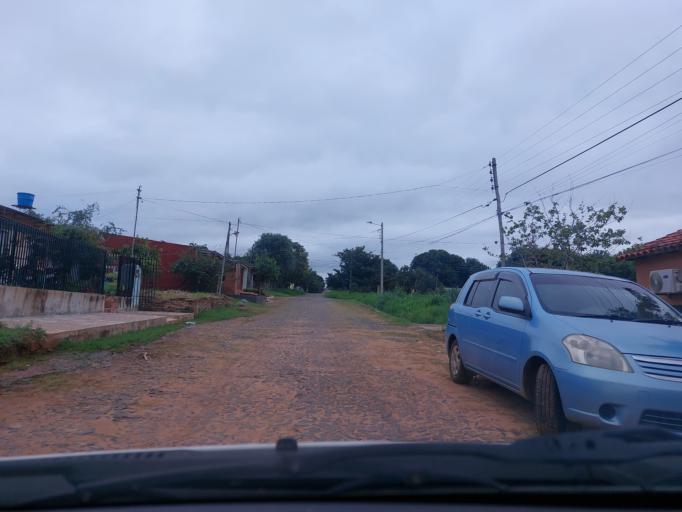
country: PY
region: San Pedro
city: Guayaybi
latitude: -24.6686
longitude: -56.4366
